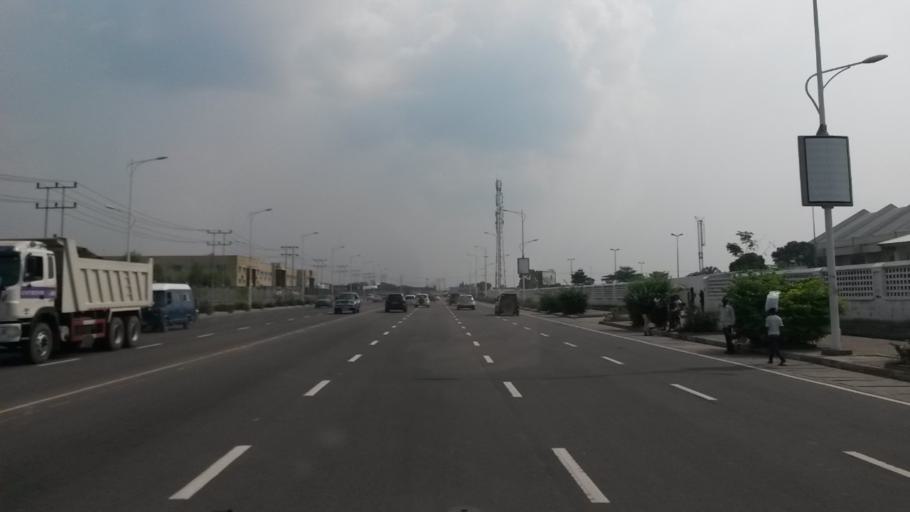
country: CD
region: Kinshasa
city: Kinshasa
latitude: -4.3363
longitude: 15.2987
